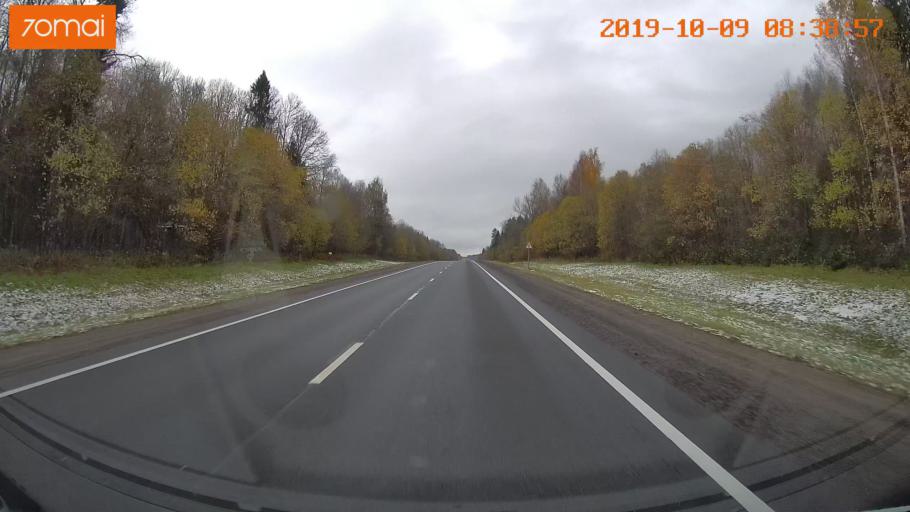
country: RU
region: Vologda
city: Gryazovets
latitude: 58.9642
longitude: 40.1592
